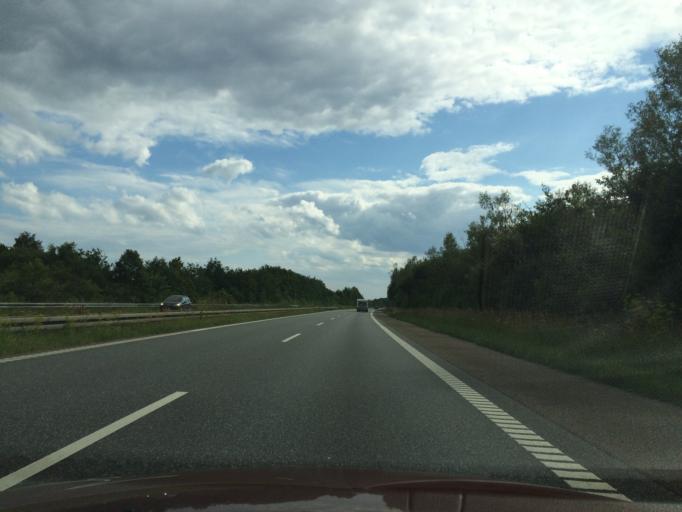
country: DK
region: Central Jutland
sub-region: Arhus Kommune
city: Logten
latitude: 56.2674
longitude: 10.3289
